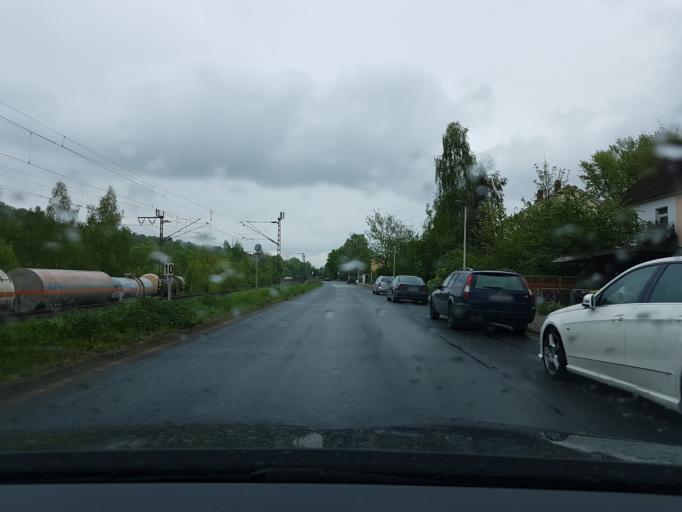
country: DE
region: Lower Saxony
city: Hameln
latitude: 52.1061
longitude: 9.3962
